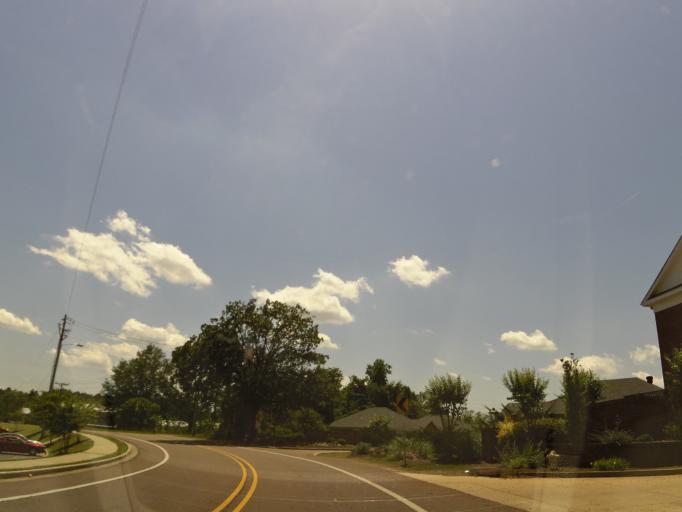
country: US
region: Mississippi
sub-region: Lafayette County
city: University
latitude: 34.3497
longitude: -89.5414
